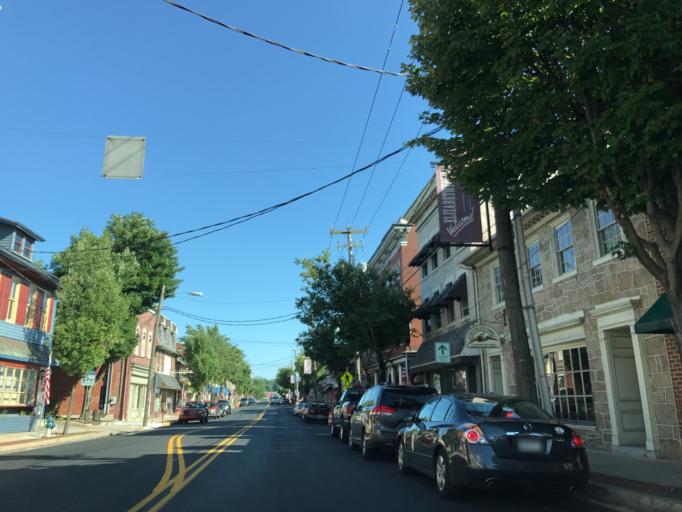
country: US
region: Pennsylvania
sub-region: Lancaster County
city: Elizabethtown
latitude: 40.1511
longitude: -76.6057
